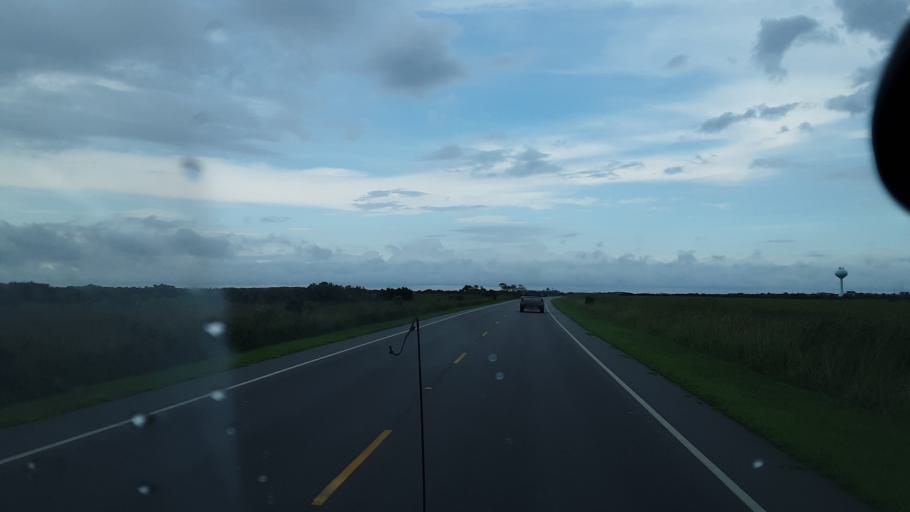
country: US
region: North Carolina
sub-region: Dare County
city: Wanchese
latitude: 35.8515
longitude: -75.5727
